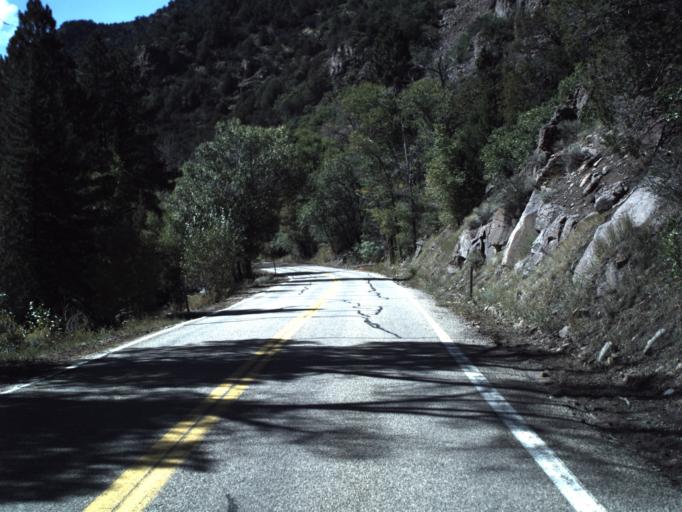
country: US
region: Utah
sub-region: Beaver County
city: Beaver
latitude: 38.2632
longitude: -112.4975
